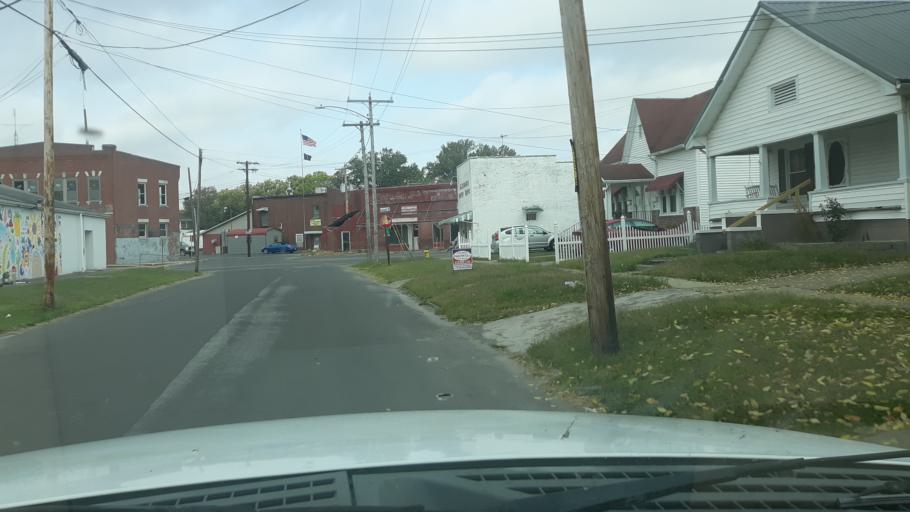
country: US
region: Illinois
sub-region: Saline County
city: Eldorado
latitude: 37.8138
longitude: -88.4369
